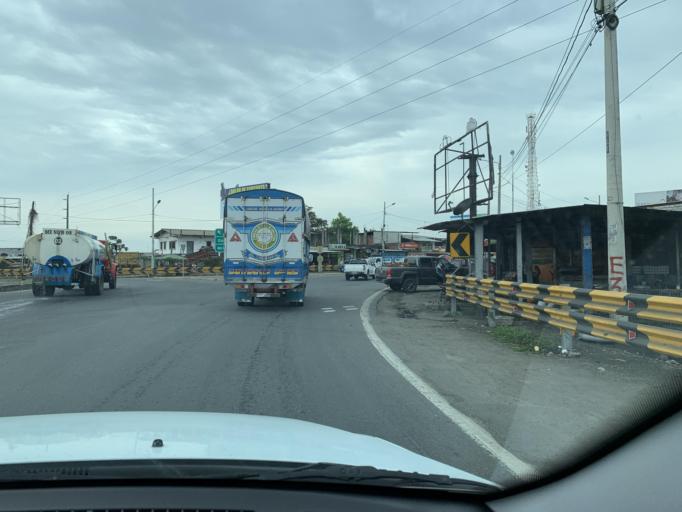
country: EC
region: Guayas
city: Yaguachi Nuevo
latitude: -2.2519
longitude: -79.6354
